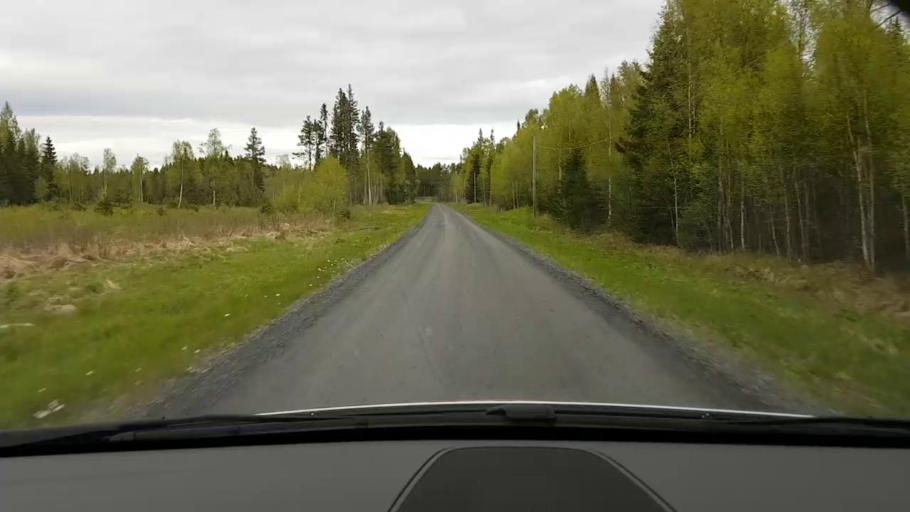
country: SE
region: Jaemtland
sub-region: Krokoms Kommun
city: Krokom
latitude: 63.2908
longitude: 14.3881
